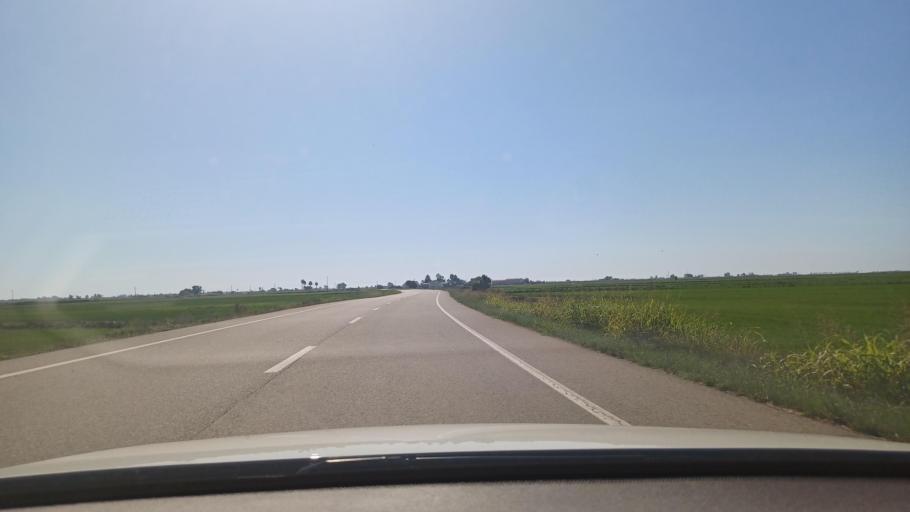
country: ES
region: Catalonia
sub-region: Provincia de Tarragona
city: Deltebre
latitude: 40.7028
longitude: 0.6648
